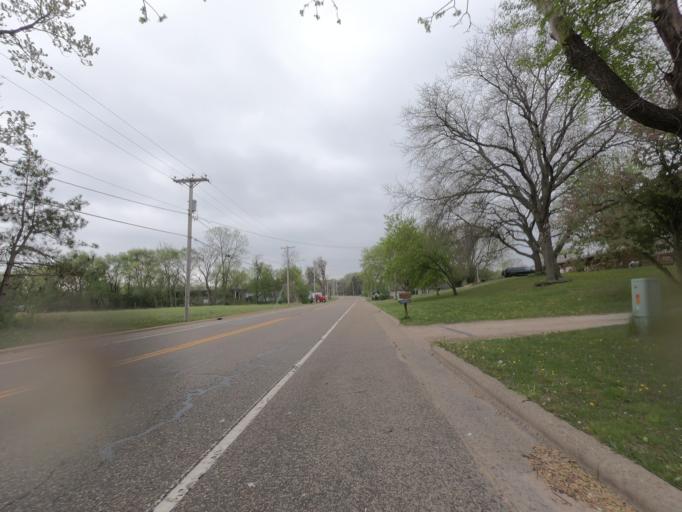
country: US
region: Wisconsin
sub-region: Jefferson County
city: Jefferson
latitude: 43.0198
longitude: -88.8105
